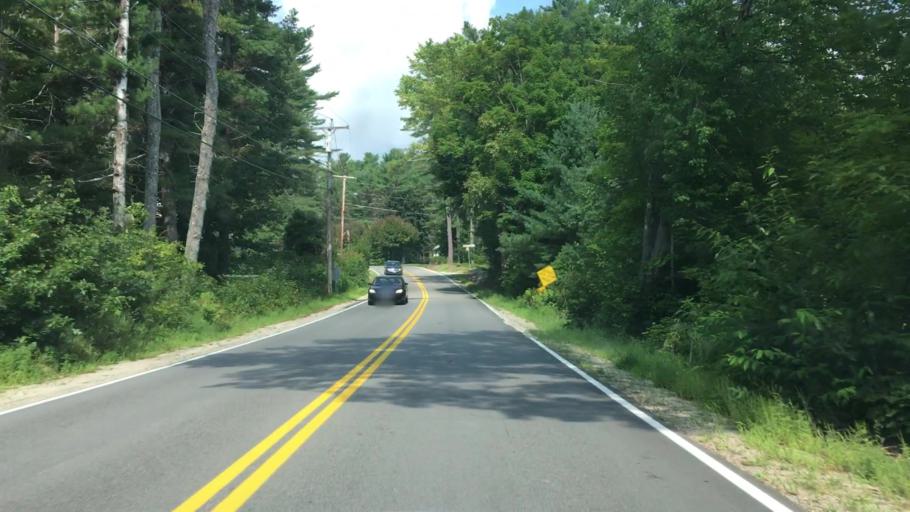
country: US
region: Maine
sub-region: Cumberland County
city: Raymond
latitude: 43.9013
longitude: -70.4595
